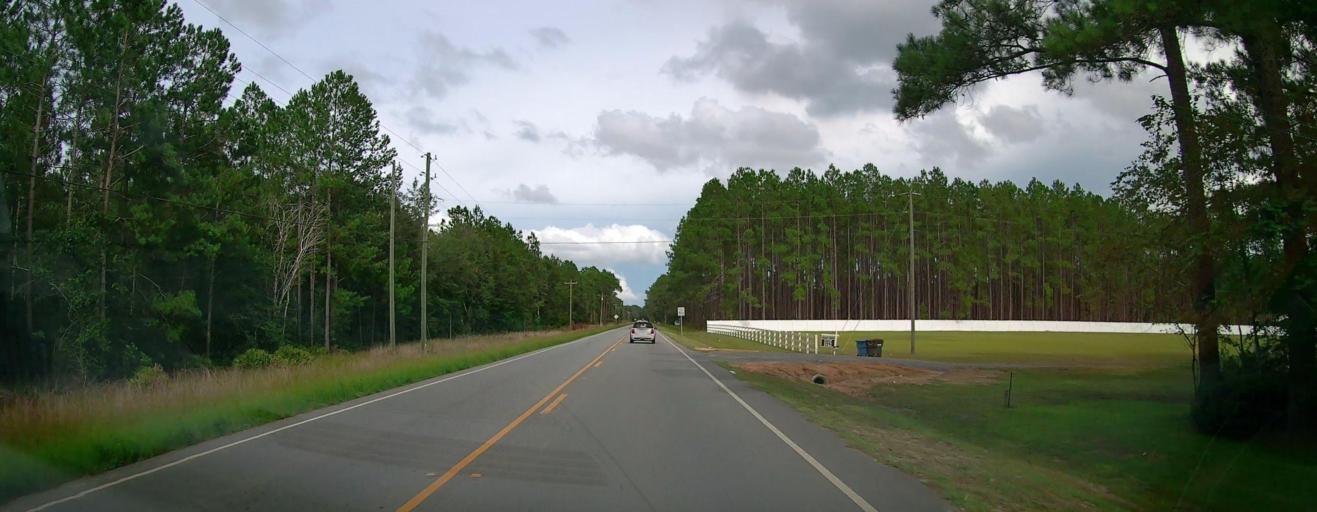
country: US
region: Georgia
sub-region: Wayne County
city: Jesup
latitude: 31.6664
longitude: -81.8727
